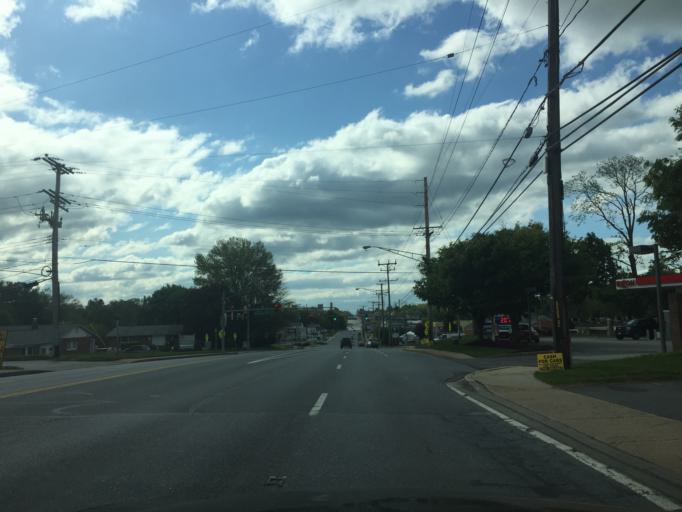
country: US
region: Maryland
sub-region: Baltimore County
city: Reisterstown
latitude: 39.4479
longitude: -76.8153
